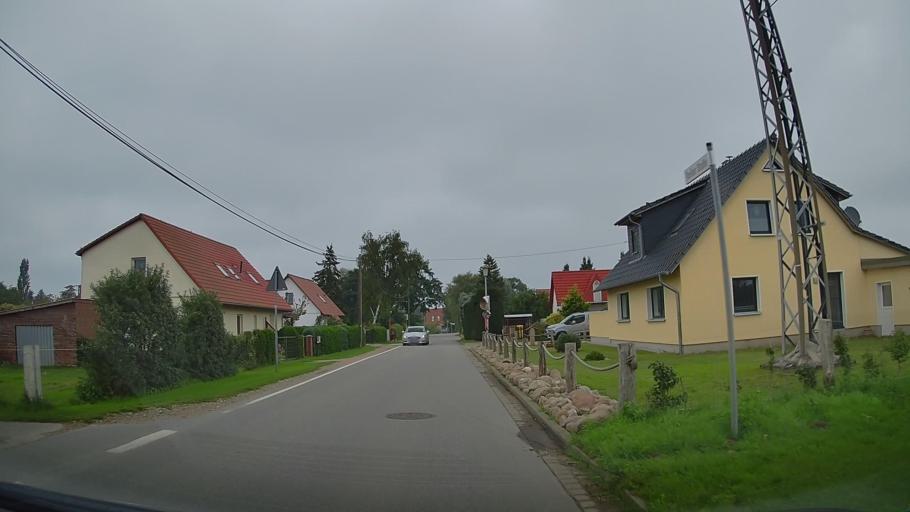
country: DE
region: Mecklenburg-Vorpommern
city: Neubukow
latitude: 54.0549
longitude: 11.6155
